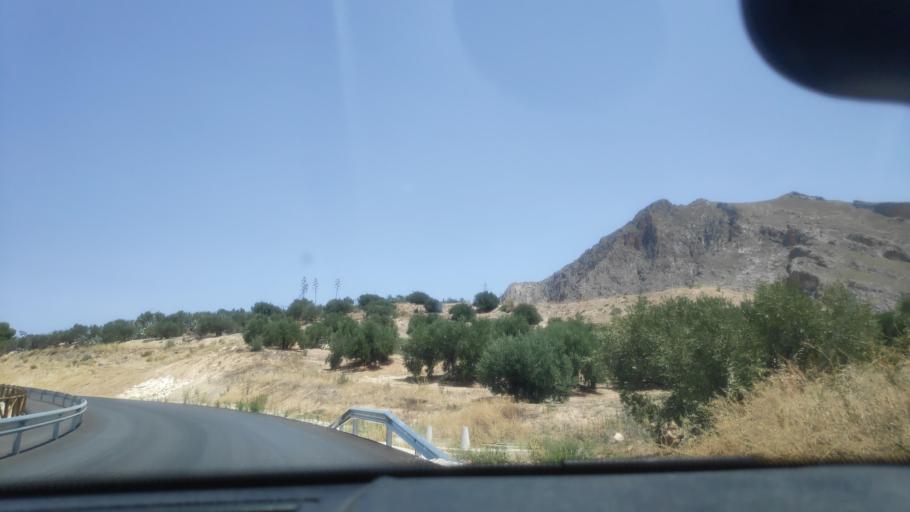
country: ES
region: Andalusia
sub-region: Provincia de Jaen
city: Jodar
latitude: 37.8118
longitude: -3.4125
